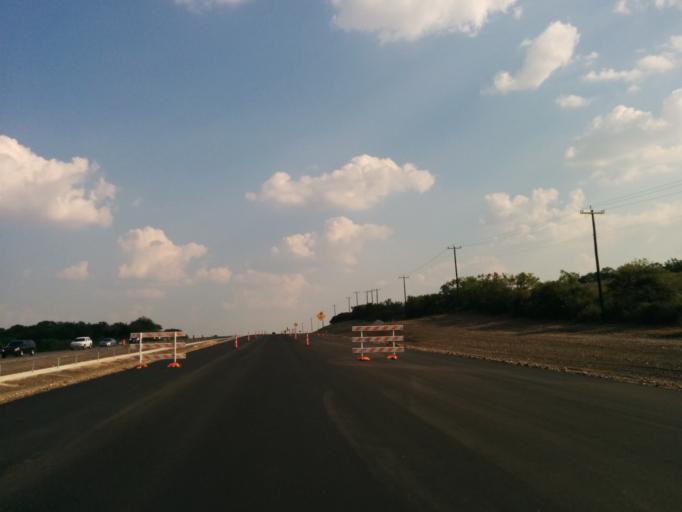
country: US
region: Texas
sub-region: Bexar County
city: Converse
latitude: 29.4736
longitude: -98.2949
